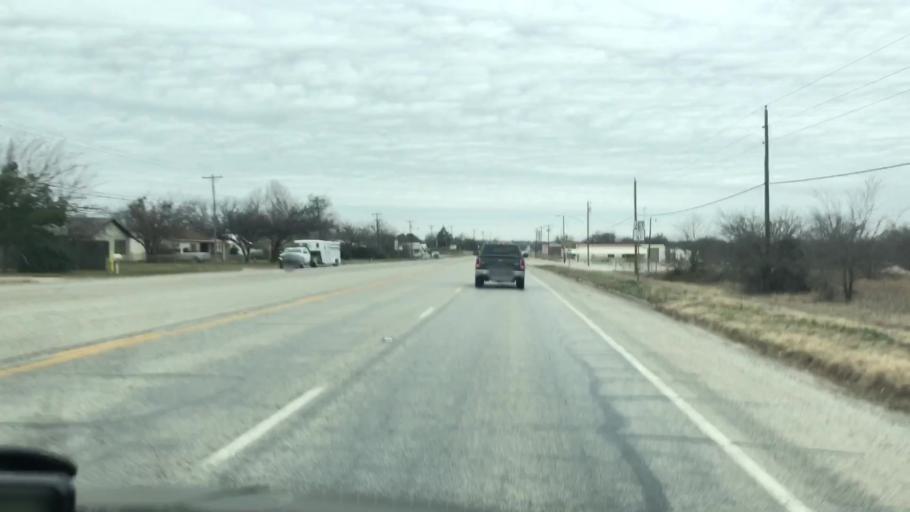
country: US
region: Texas
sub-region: Jack County
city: Jacksboro
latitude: 33.2047
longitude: -98.1526
